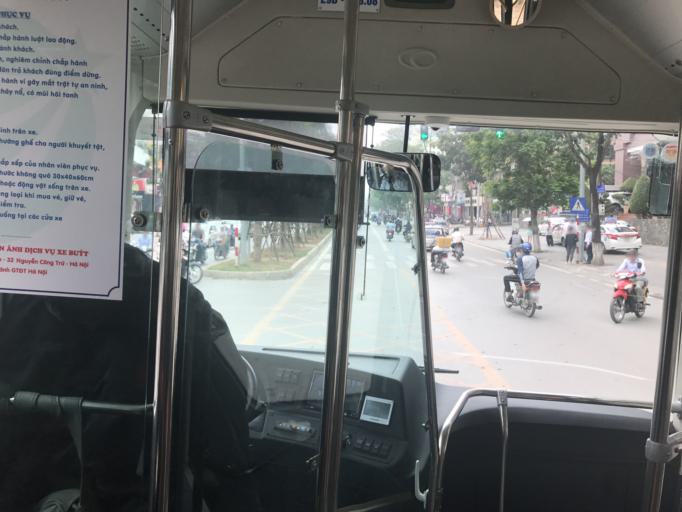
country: VN
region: Ha Noi
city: Dong Da
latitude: 21.0221
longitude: 105.8190
